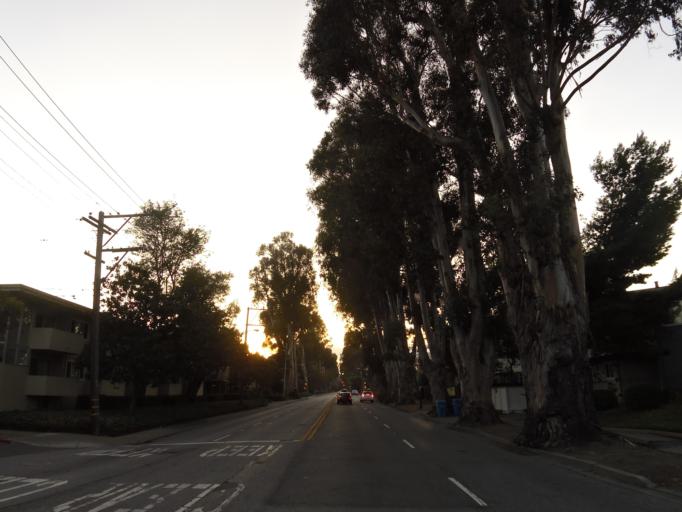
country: US
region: California
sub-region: San Mateo County
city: Burlingame
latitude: 37.5754
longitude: -122.3463
